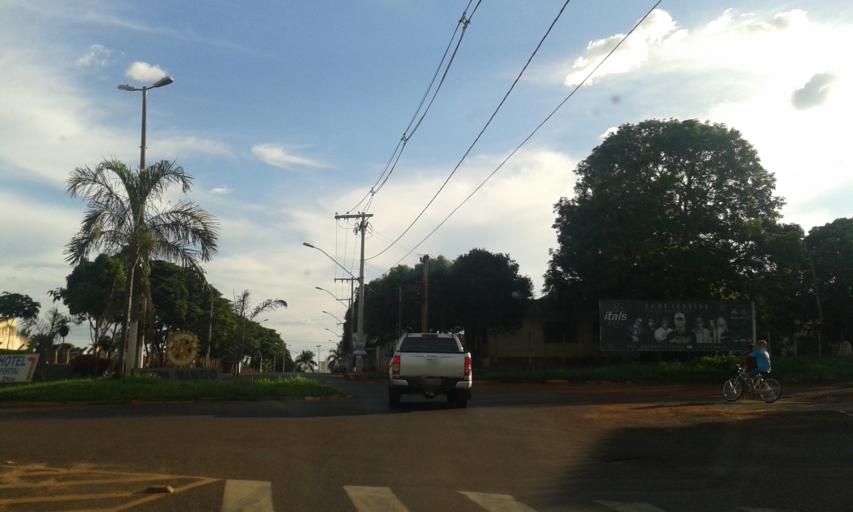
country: BR
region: Minas Gerais
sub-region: Ituiutaba
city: Ituiutaba
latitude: -18.9586
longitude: -49.4572
